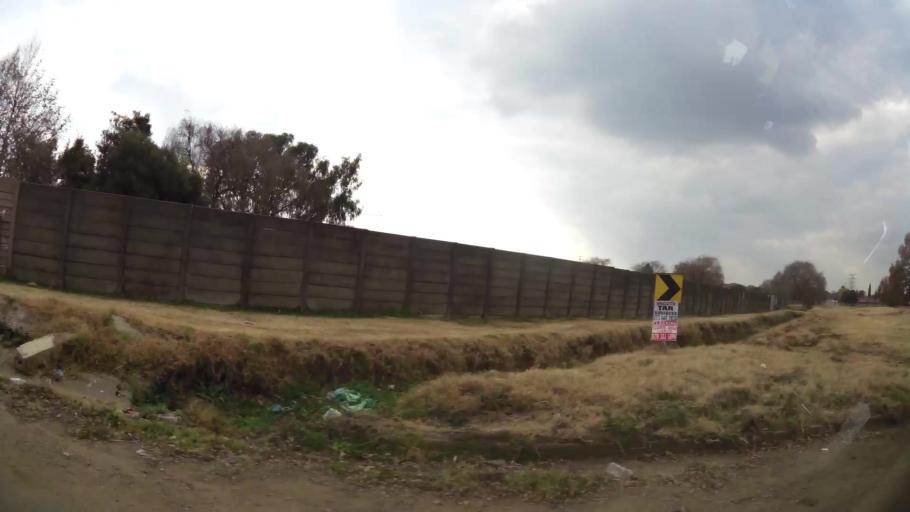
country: ZA
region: Gauteng
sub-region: Ekurhuleni Metropolitan Municipality
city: Benoni
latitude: -26.1198
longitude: 28.3654
